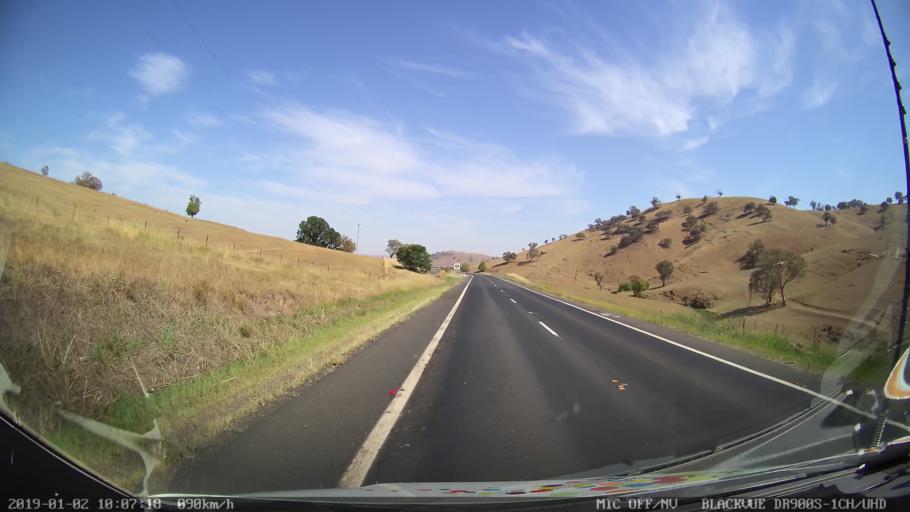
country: AU
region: New South Wales
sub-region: Gundagai
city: Gundagai
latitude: -35.1394
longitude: 148.1142
